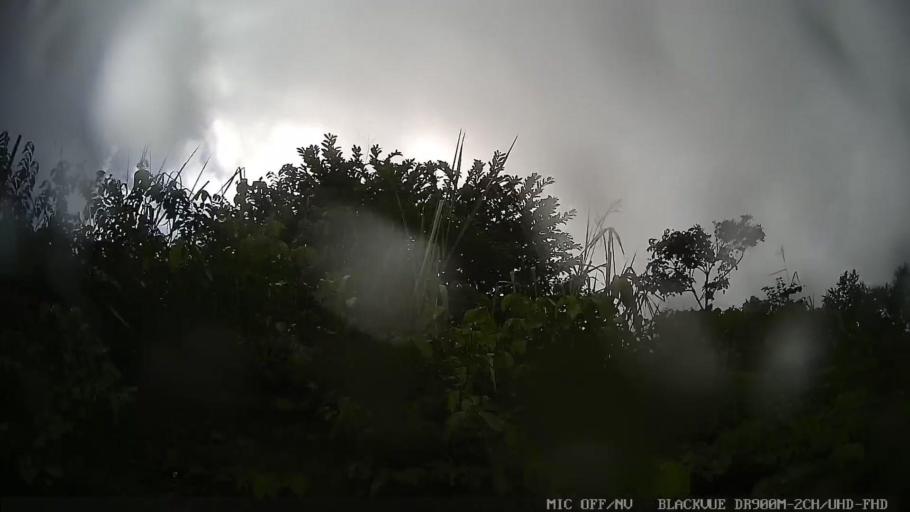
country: BR
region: Sao Paulo
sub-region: Peruibe
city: Peruibe
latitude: -24.2500
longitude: -46.9000
